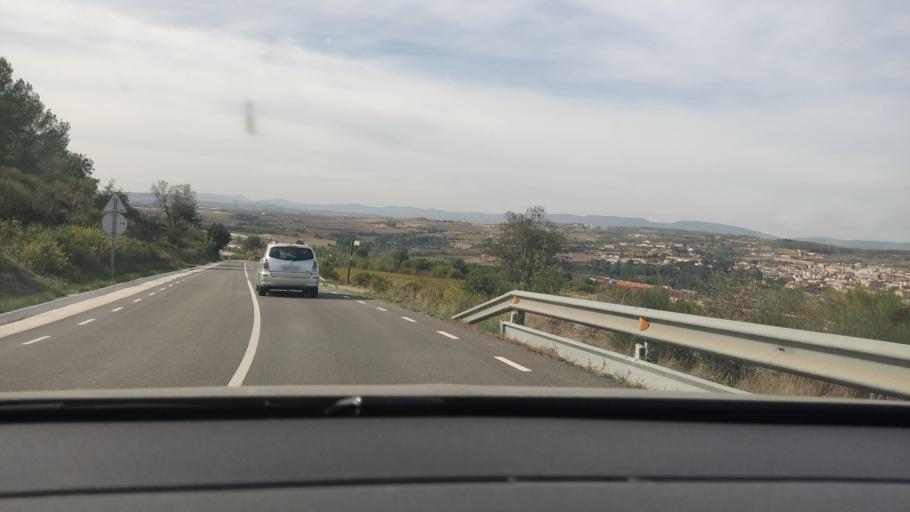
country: ES
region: Catalonia
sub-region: Provincia de Barcelona
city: Sant Sadurni d'Anoia
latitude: 41.4180
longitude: 1.7996
